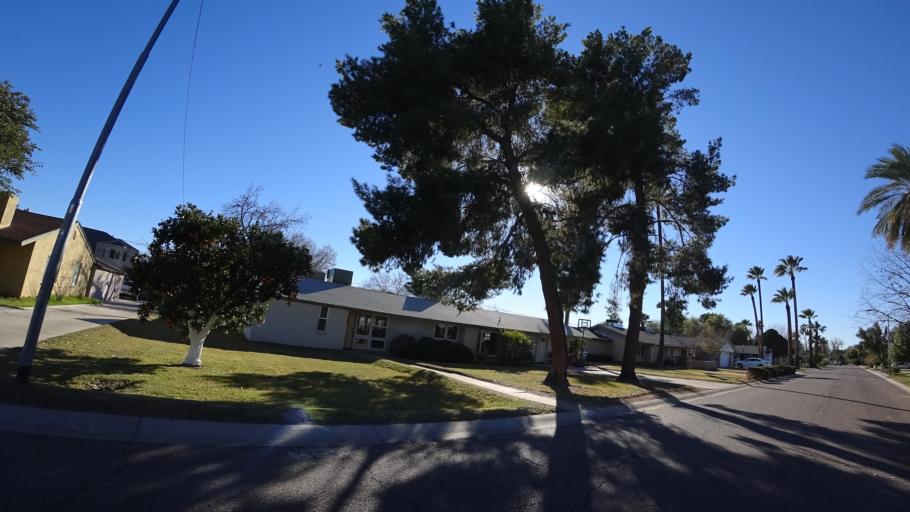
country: US
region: Arizona
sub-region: Maricopa County
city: Phoenix
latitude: 33.5187
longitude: -112.0495
